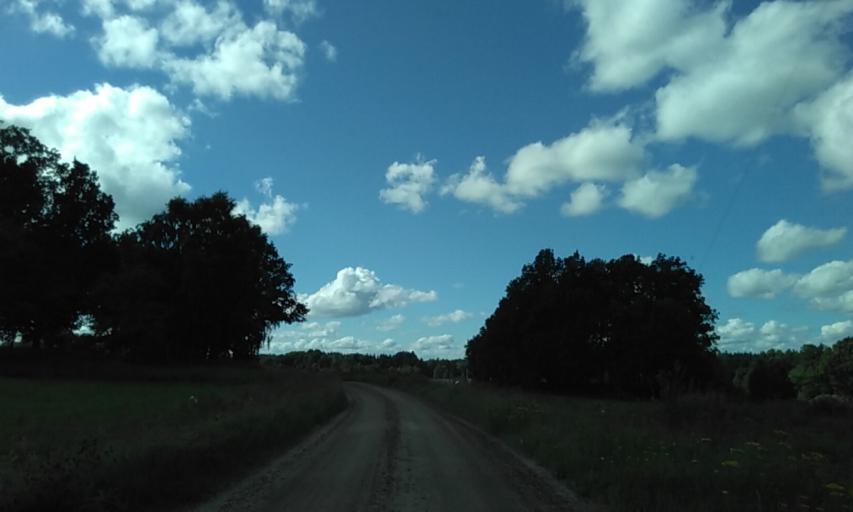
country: SE
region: Vaestra Goetaland
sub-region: Vargarda Kommun
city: Vargarda
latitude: 58.0061
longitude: 12.8872
